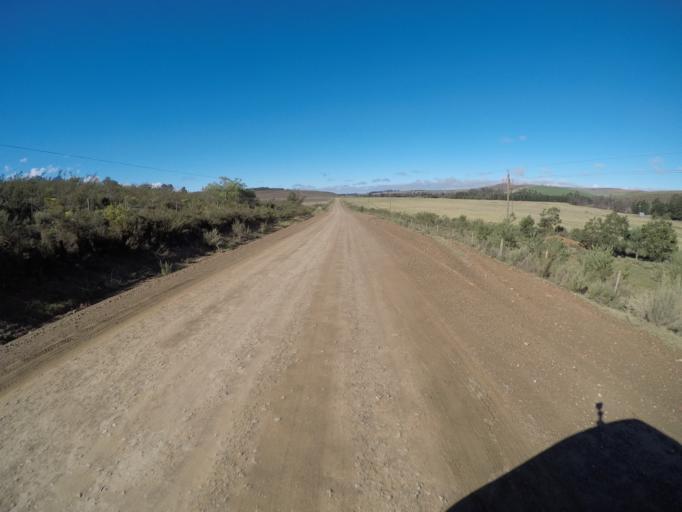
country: ZA
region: Western Cape
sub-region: Overberg District Municipality
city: Caledon
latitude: -34.0844
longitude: 19.6499
